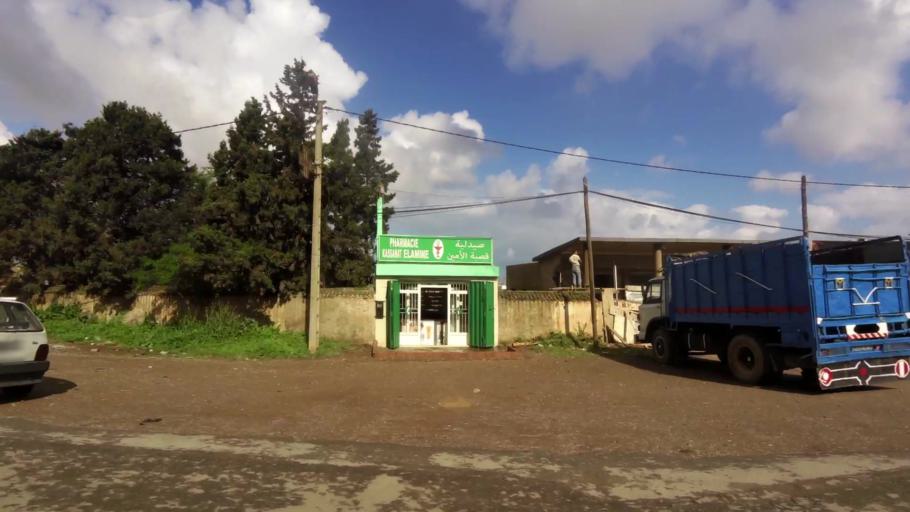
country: MA
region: Grand Casablanca
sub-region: Nouaceur
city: Bouskoura
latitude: 33.5334
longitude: -7.6857
